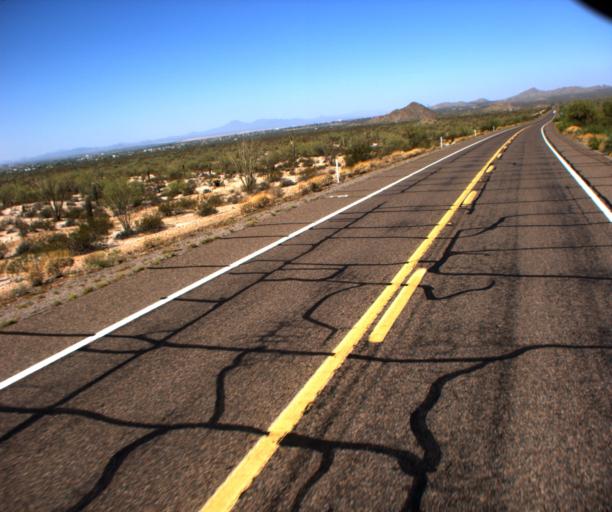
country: US
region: Arizona
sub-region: Pinal County
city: Sacaton
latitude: 33.0061
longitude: -111.7081
